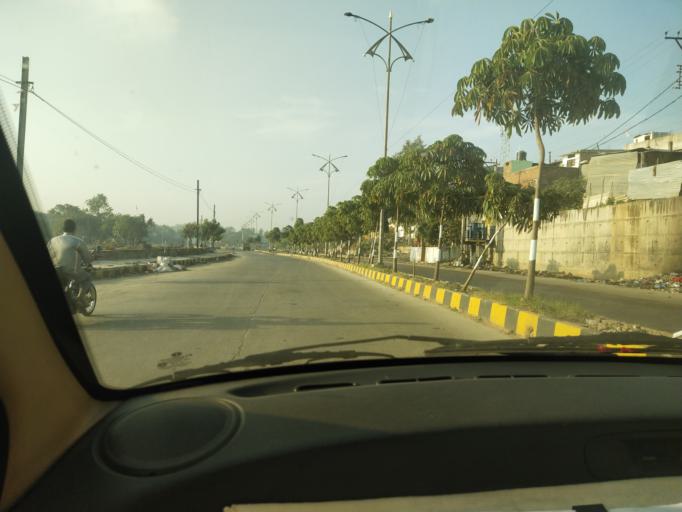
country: IN
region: Telangana
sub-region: Hyderabad
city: Hyderabad
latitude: 17.3659
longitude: 78.4557
